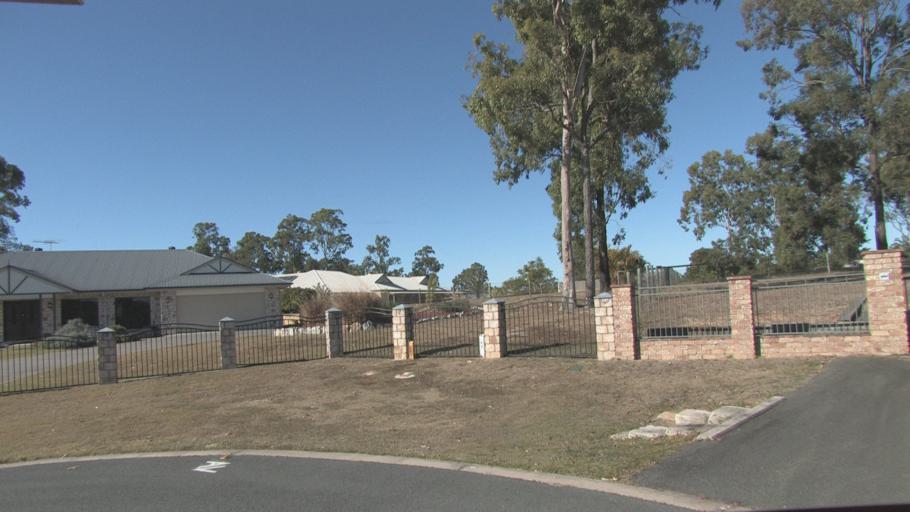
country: AU
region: Queensland
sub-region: Logan
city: North Maclean
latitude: -27.7534
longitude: 152.9613
